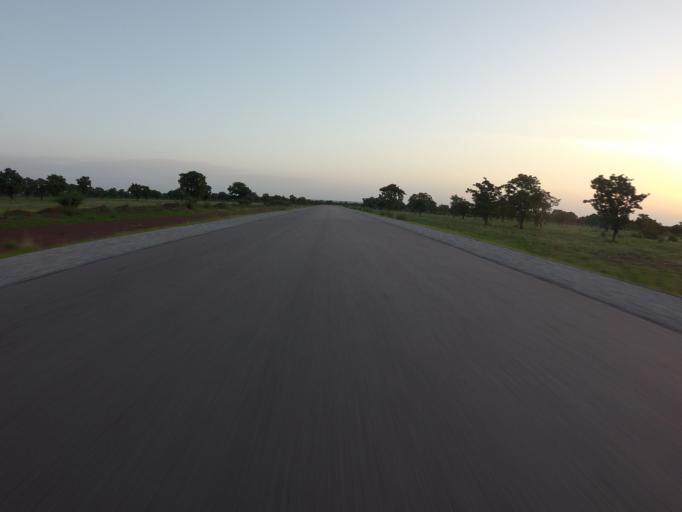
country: GH
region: Northern
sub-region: Yendi
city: Yendi
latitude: 9.9416
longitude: -0.1667
